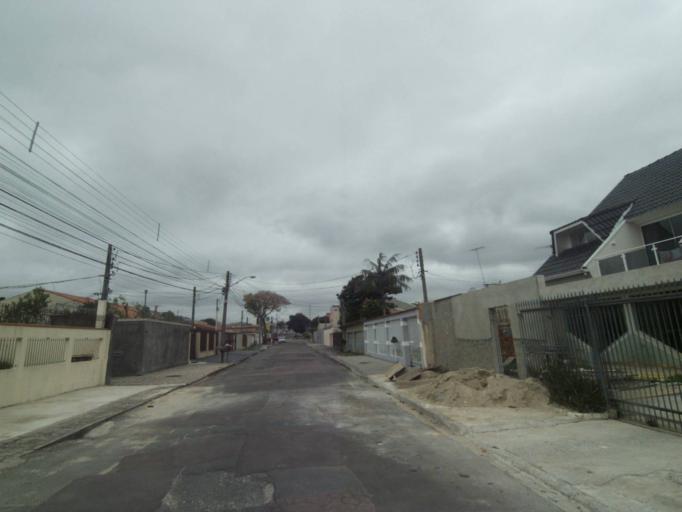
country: BR
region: Parana
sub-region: Curitiba
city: Curitiba
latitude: -25.4674
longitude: -49.2719
